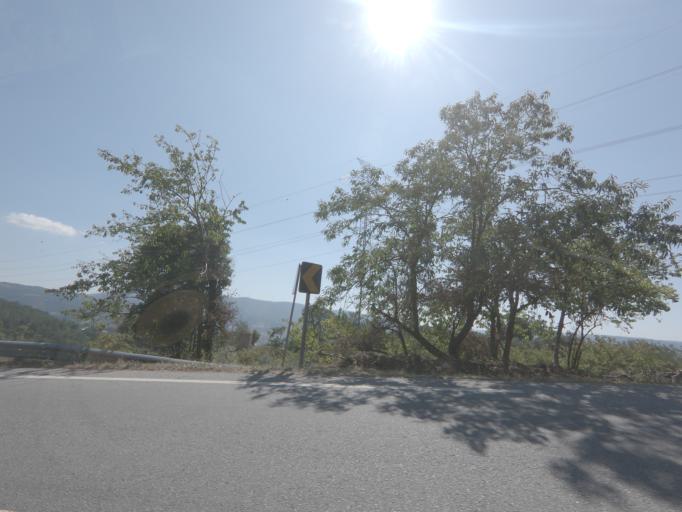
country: PT
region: Viseu
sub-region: Tarouca
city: Tarouca
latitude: 41.0391
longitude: -7.7416
